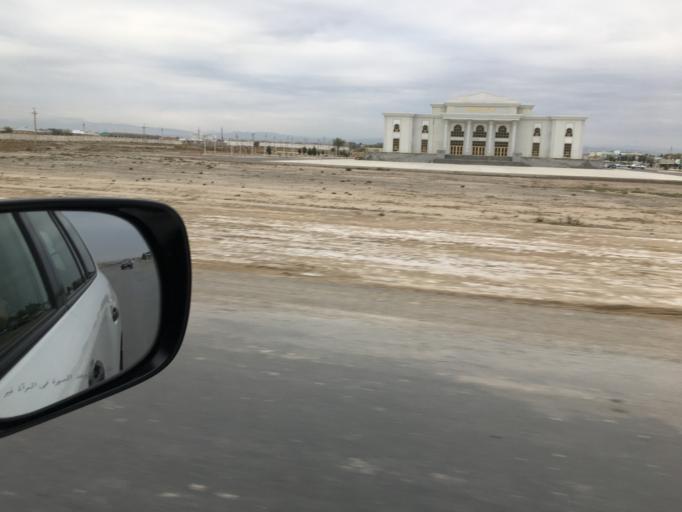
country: TM
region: Ahal
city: Kaka
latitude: 37.3624
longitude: 59.6277
